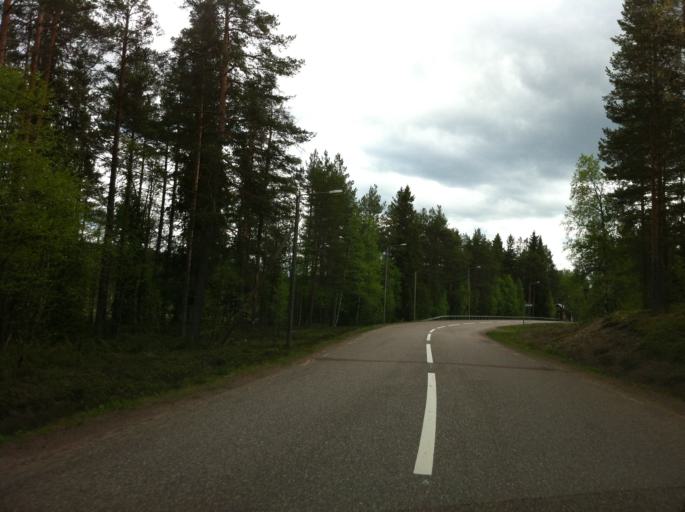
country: NO
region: Hedmark
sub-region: Trysil
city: Innbygda
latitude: 61.4170
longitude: 13.0858
